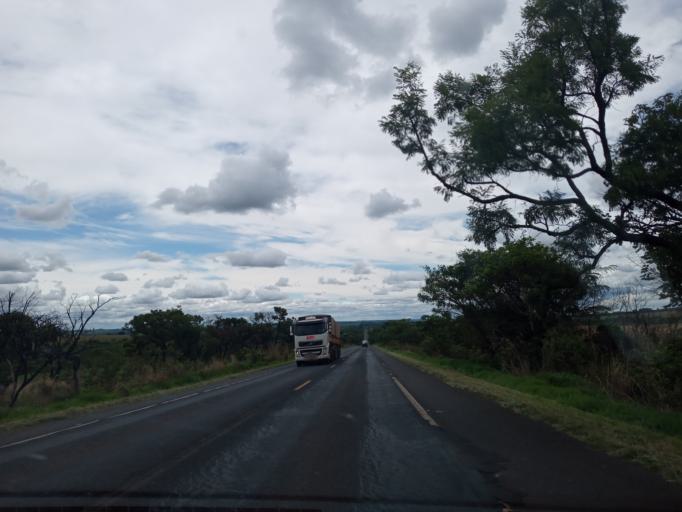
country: BR
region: Minas Gerais
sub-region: Uberlandia
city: Uberlandia
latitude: -19.1894
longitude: -47.8699
